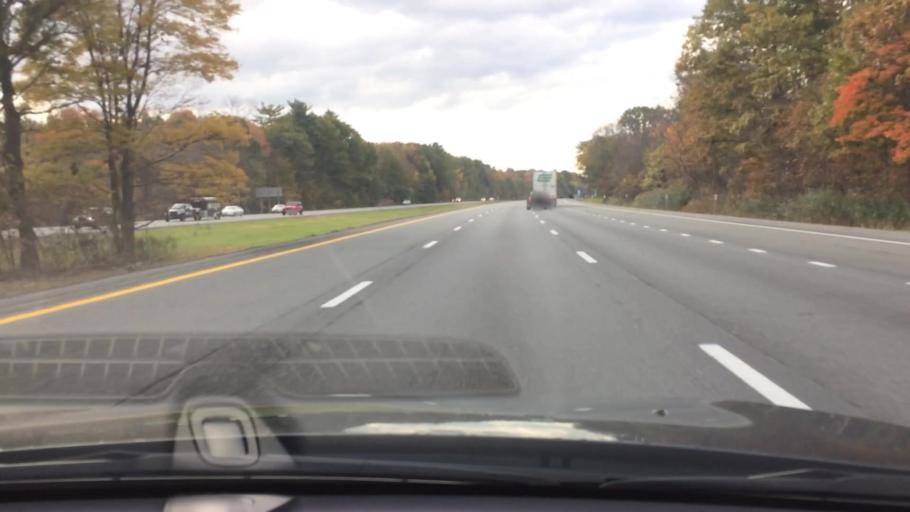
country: US
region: New York
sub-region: Saratoga County
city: Country Knolls
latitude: 42.9646
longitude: -73.8016
